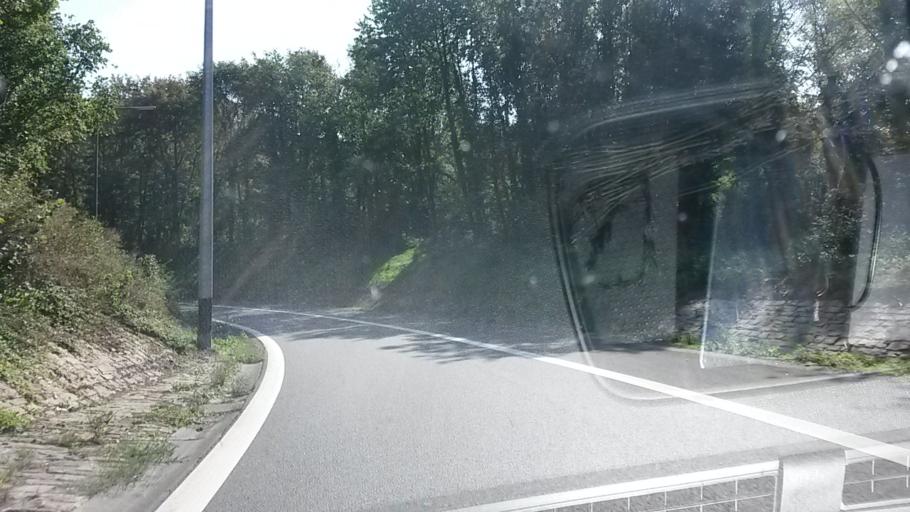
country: BE
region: Wallonia
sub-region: Province du Hainaut
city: Anderlues
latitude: 50.3900
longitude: 4.2927
